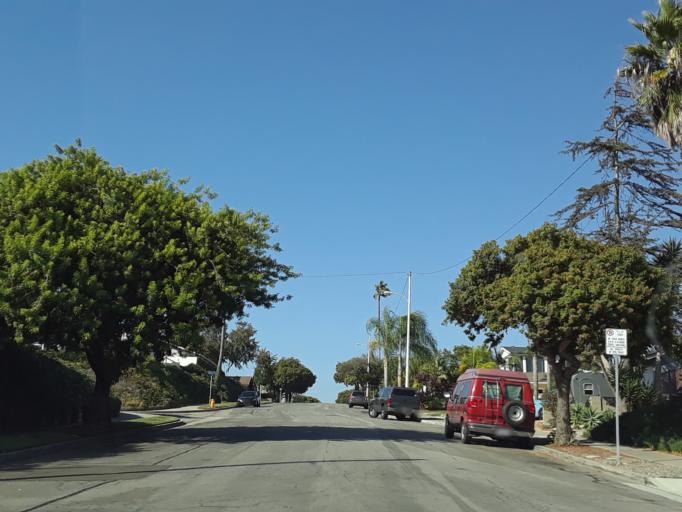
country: US
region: California
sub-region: Orange County
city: Huntington Beach
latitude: 33.6798
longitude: -117.9826
